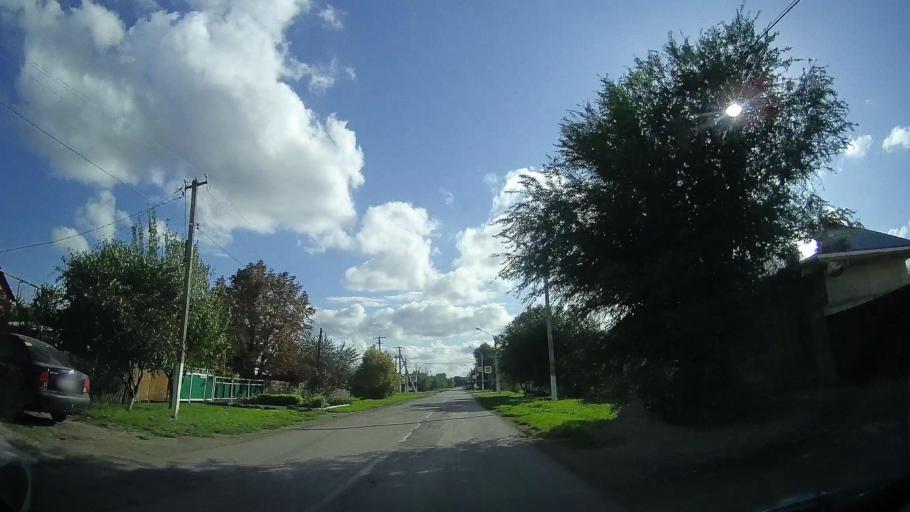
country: RU
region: Rostov
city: Tselina
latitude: 46.5348
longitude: 41.0338
